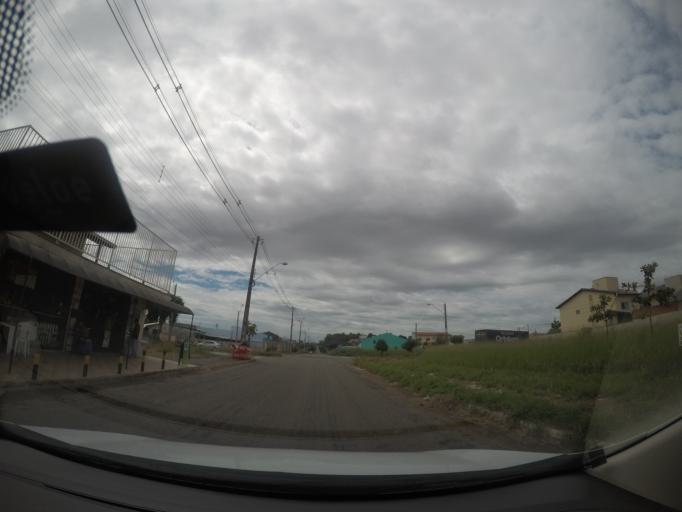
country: BR
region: Goias
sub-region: Goiania
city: Goiania
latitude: -16.7241
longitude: -49.3490
